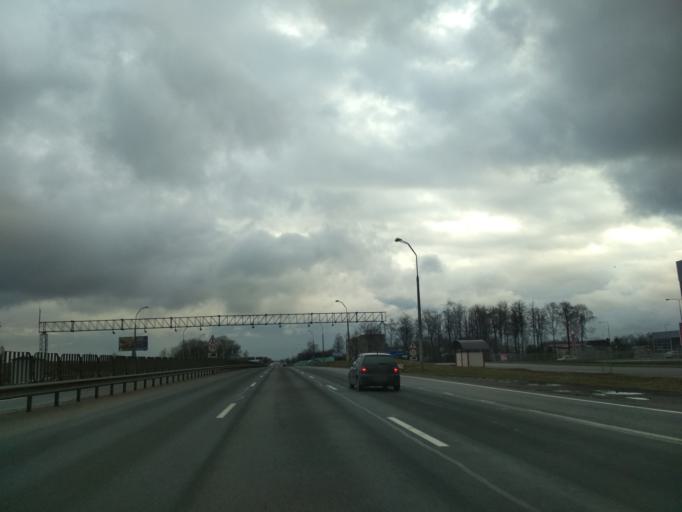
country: BY
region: Minsk
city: Pryvol'ny
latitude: 53.8024
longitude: 27.7984
